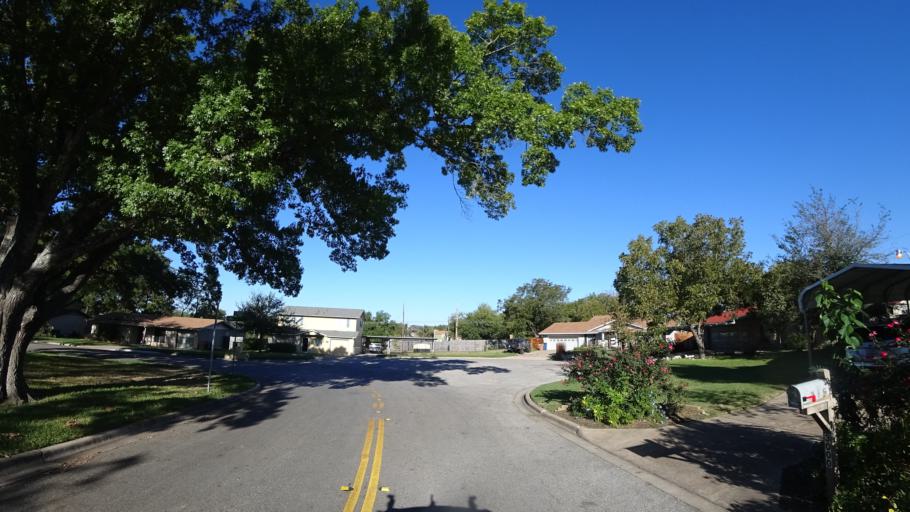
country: US
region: Texas
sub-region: Travis County
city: Austin
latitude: 30.3054
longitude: -97.6777
